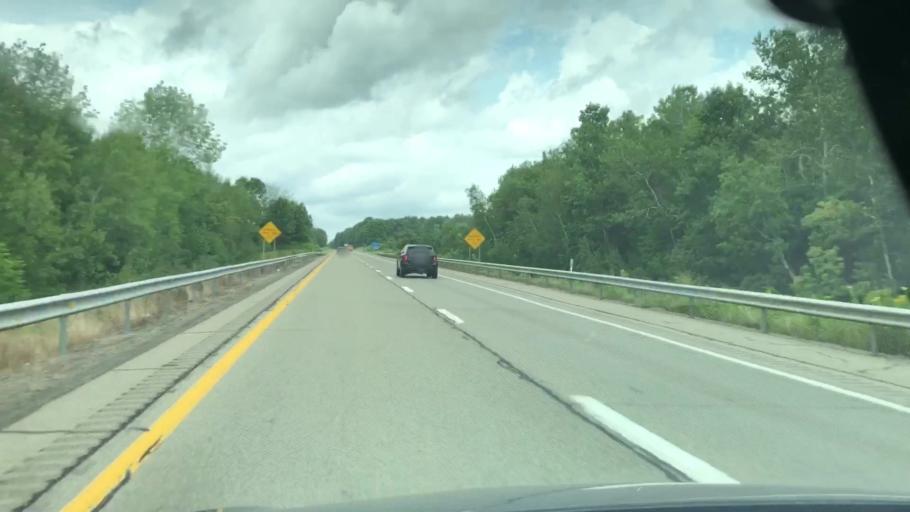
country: US
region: Pennsylvania
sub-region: Erie County
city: Edinboro
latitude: 41.8213
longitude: -80.1752
